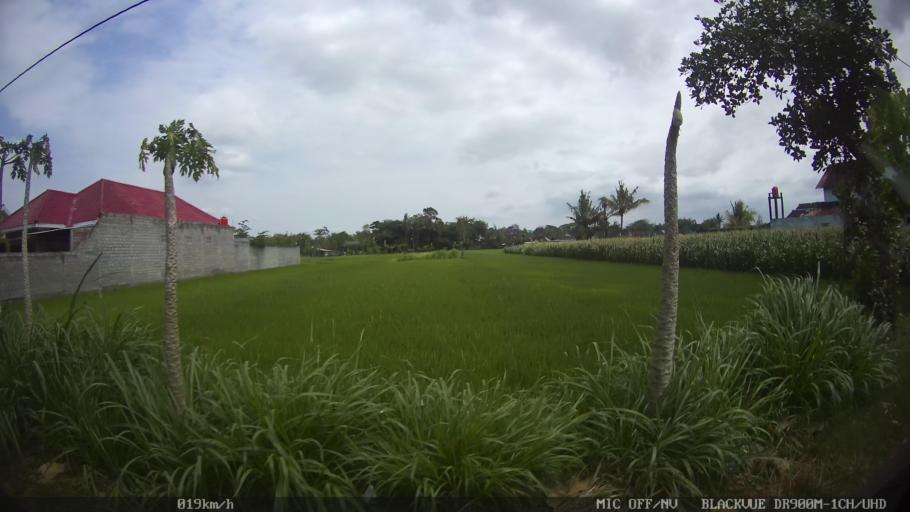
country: ID
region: Central Java
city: Candi Prambanan
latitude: -7.8120
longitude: 110.5002
